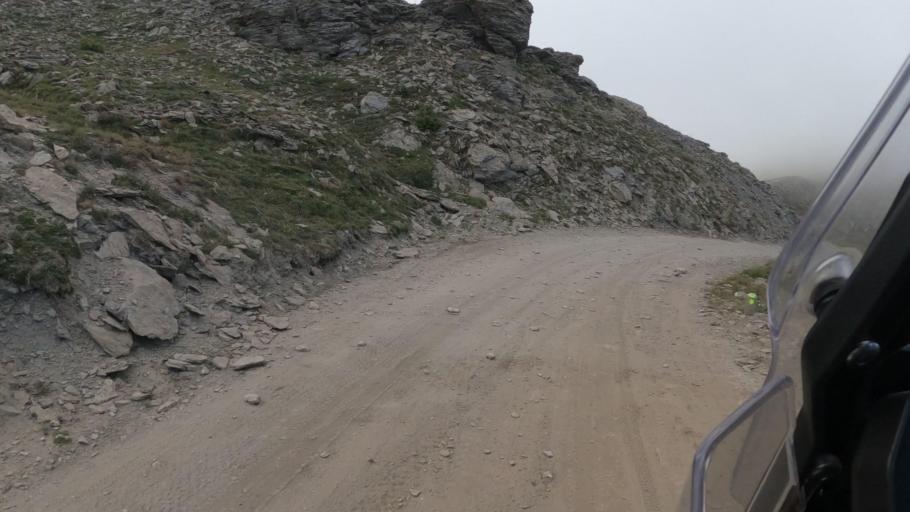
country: IT
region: Piedmont
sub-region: Provincia di Torino
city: Pragelato-Rua
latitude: 45.0487
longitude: 6.9335
